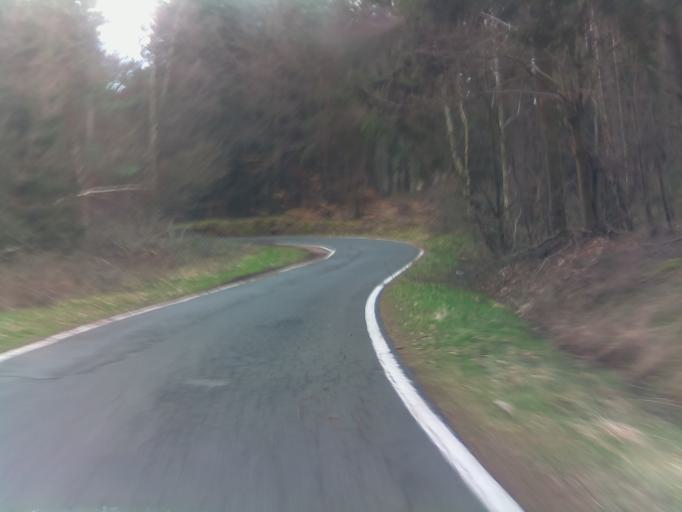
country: DE
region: Rheinland-Pfalz
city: Oberheimbach
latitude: 49.9843
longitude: 7.8042
